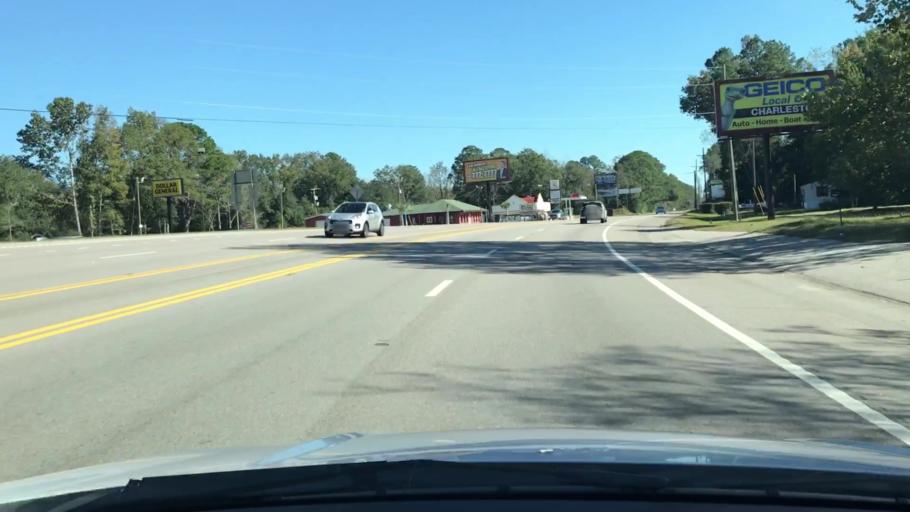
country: US
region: South Carolina
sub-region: Charleston County
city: Ravenel
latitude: 32.7736
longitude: -80.4598
